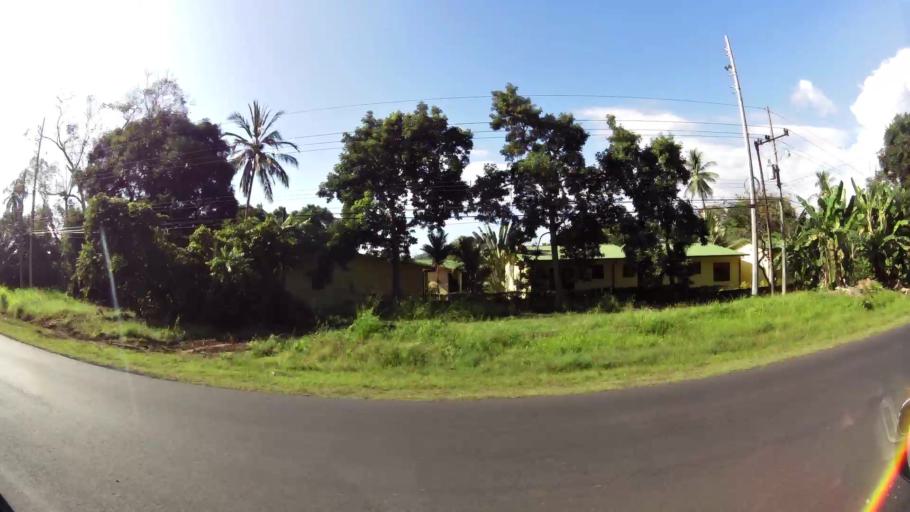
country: CR
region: Puntarenas
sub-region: Canton de Garabito
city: Jaco
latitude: 9.5984
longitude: -84.6174
